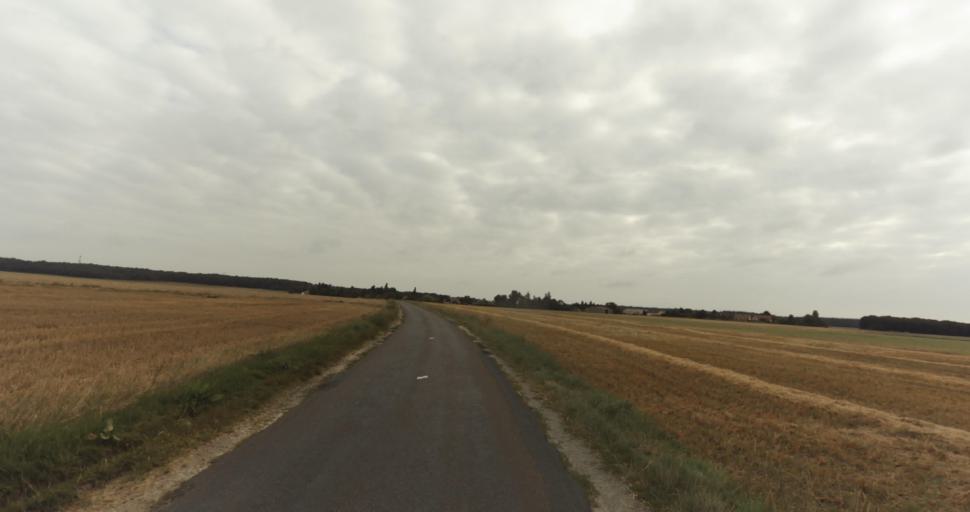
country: FR
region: Haute-Normandie
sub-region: Departement de l'Eure
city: Marcilly-sur-Eure
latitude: 48.8403
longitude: 1.3119
